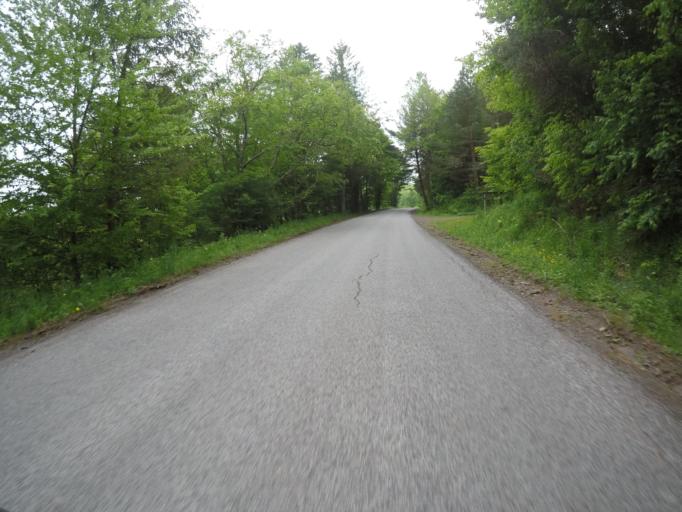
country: US
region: New York
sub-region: Delaware County
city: Stamford
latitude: 42.2629
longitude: -74.7239
